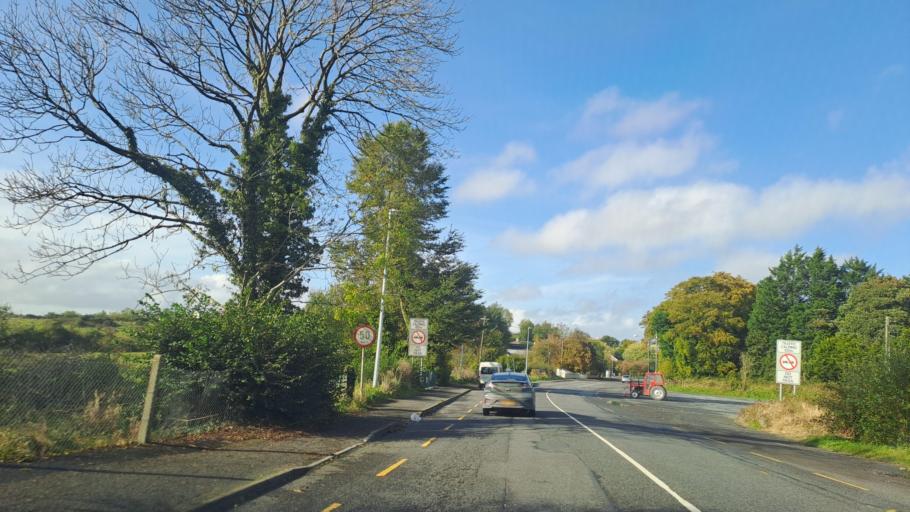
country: IE
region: Ulster
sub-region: An Cabhan
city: Cootehill
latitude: 54.0707
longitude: -7.0677
